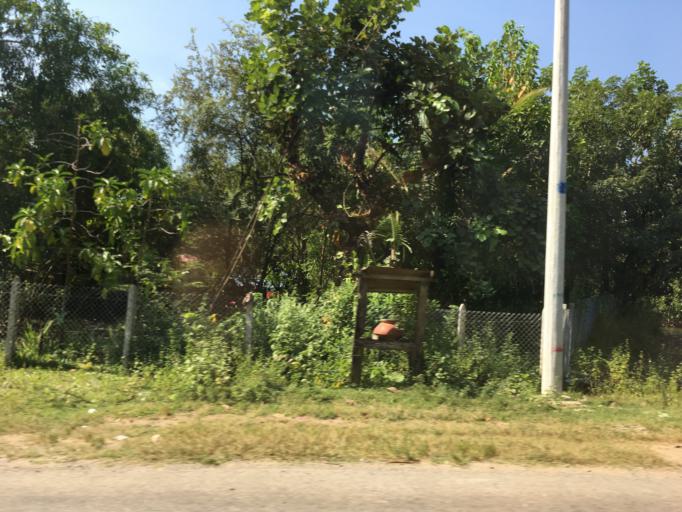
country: MM
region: Kayin
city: Hpa-an
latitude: 16.7880
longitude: 97.6856
